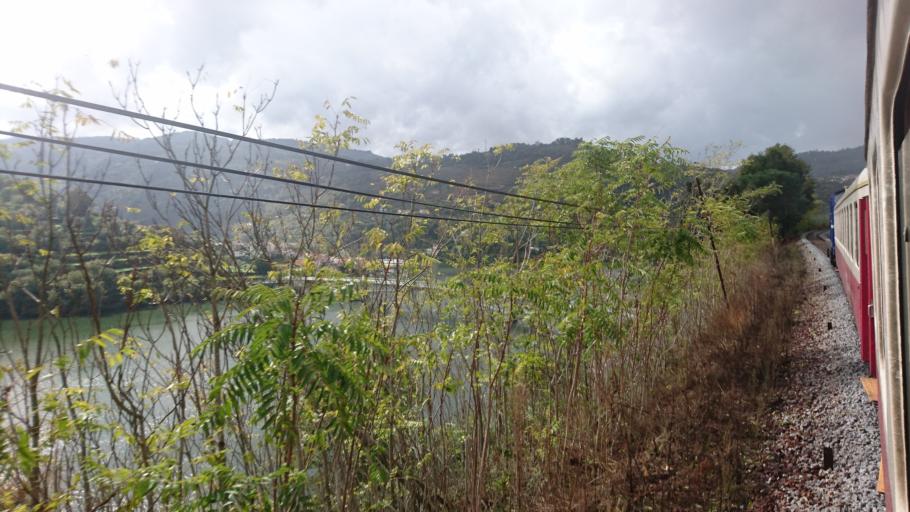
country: PT
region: Viseu
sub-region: Cinfaes
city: Cinfaes
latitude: 41.0941
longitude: -8.0754
